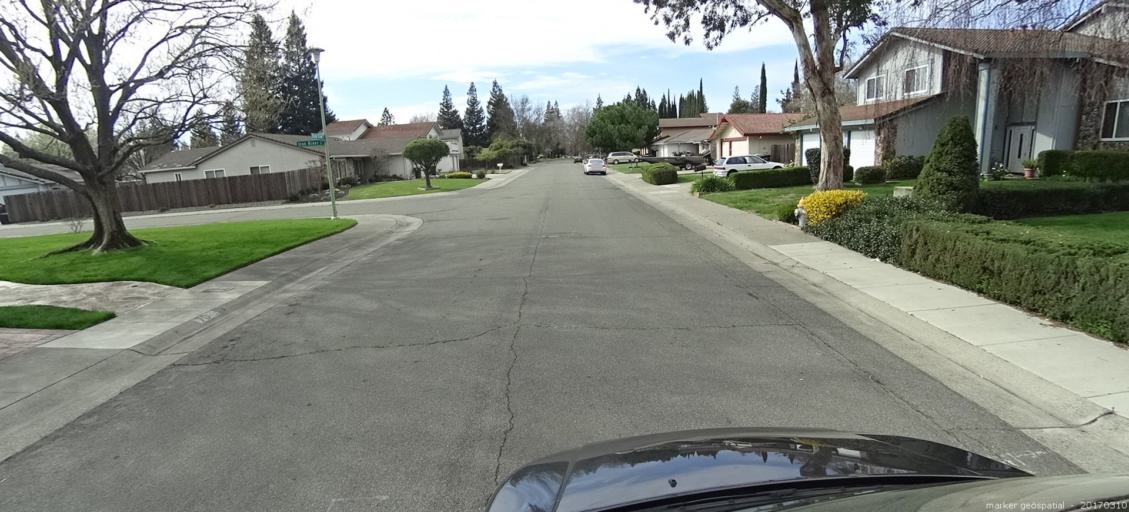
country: US
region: California
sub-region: Sacramento County
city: Parkway
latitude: 38.4935
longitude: -121.5269
